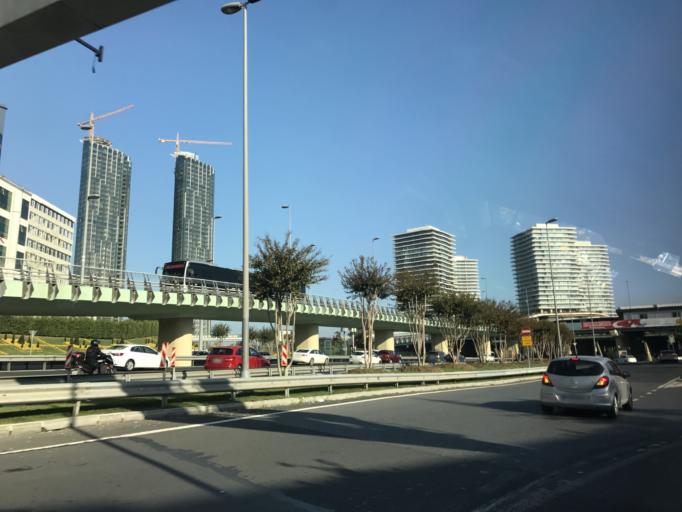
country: TR
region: Istanbul
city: Sisli
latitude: 41.0671
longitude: 29.0103
